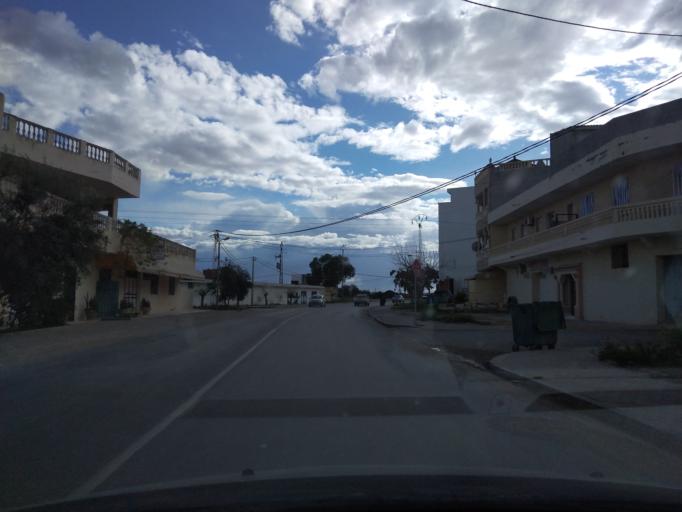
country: TN
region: Susah
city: Masakin
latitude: 35.7159
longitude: 10.5637
